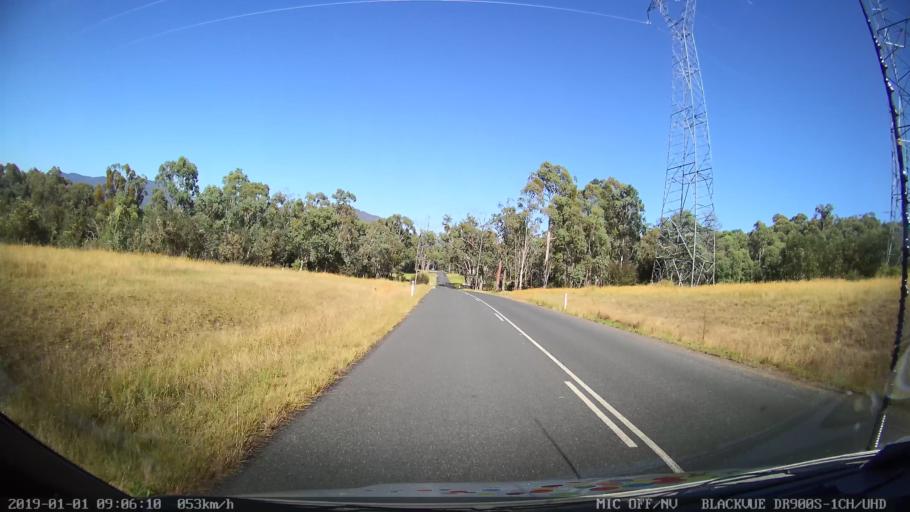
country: AU
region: New South Wales
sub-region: Snowy River
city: Jindabyne
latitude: -36.2169
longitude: 148.1413
